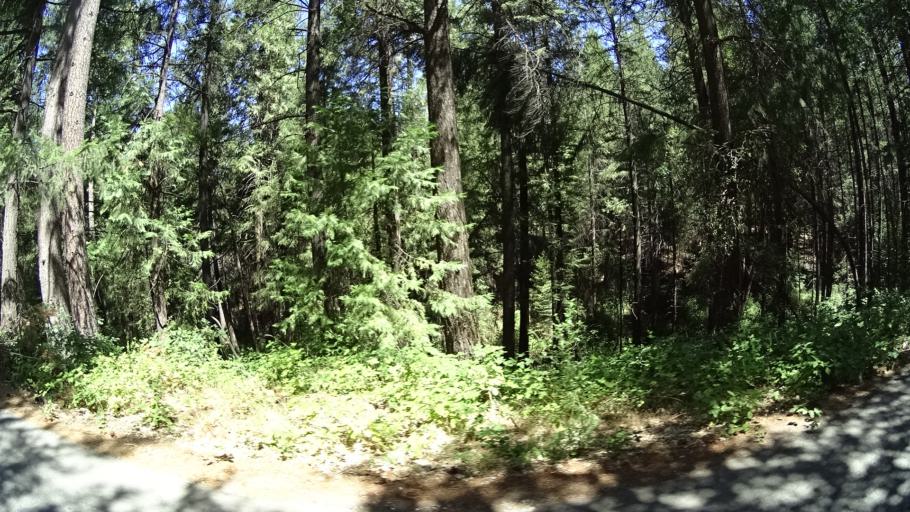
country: US
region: California
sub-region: Amador County
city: Pioneer
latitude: 38.4096
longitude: -120.5119
